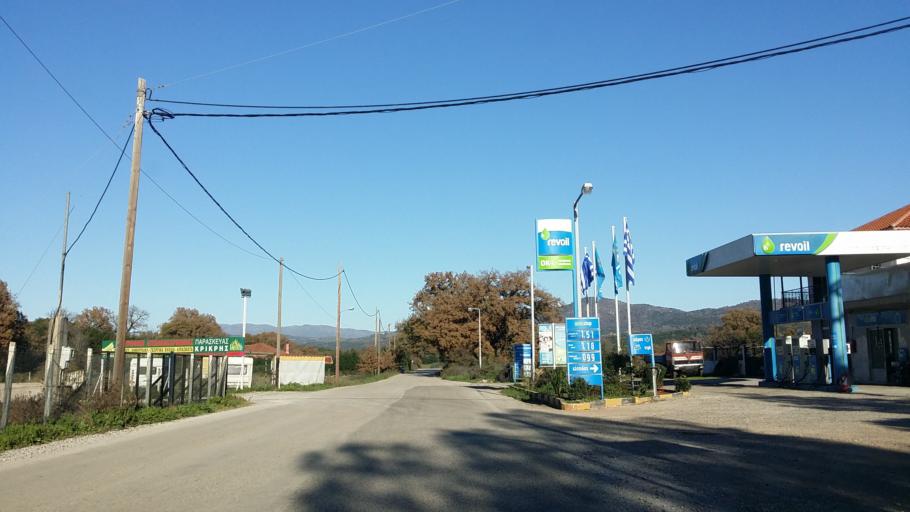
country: GR
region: West Greece
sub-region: Nomos Aitolias kai Akarnanias
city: Fitiai
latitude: 38.6176
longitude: 21.1440
